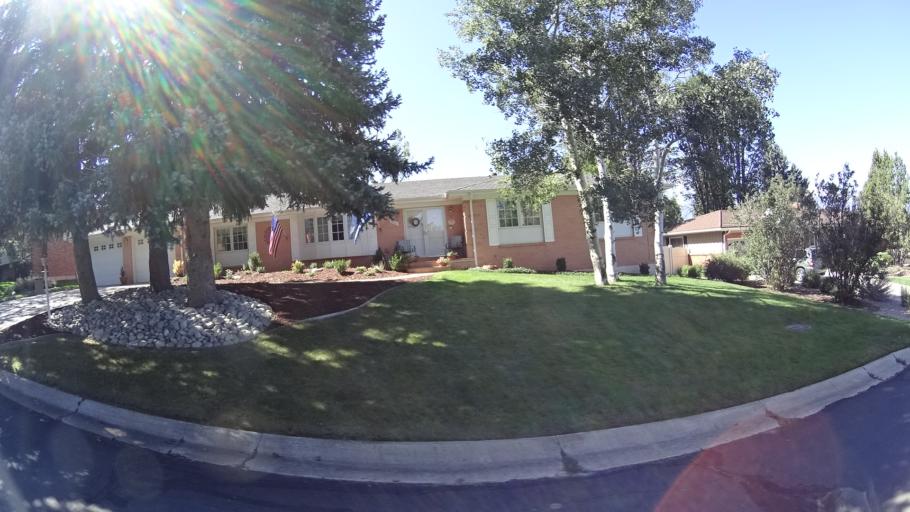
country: US
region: Colorado
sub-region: El Paso County
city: Colorado Springs
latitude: 38.8757
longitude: -104.7824
